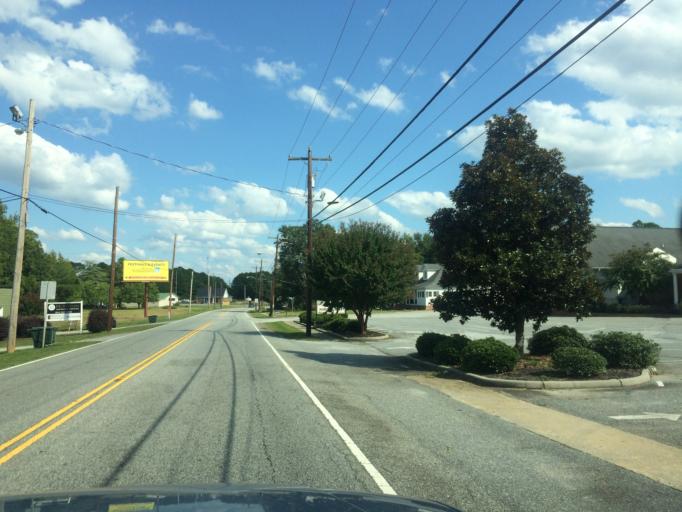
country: US
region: South Carolina
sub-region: Anderson County
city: Honea Path
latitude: 34.4537
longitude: -82.4059
